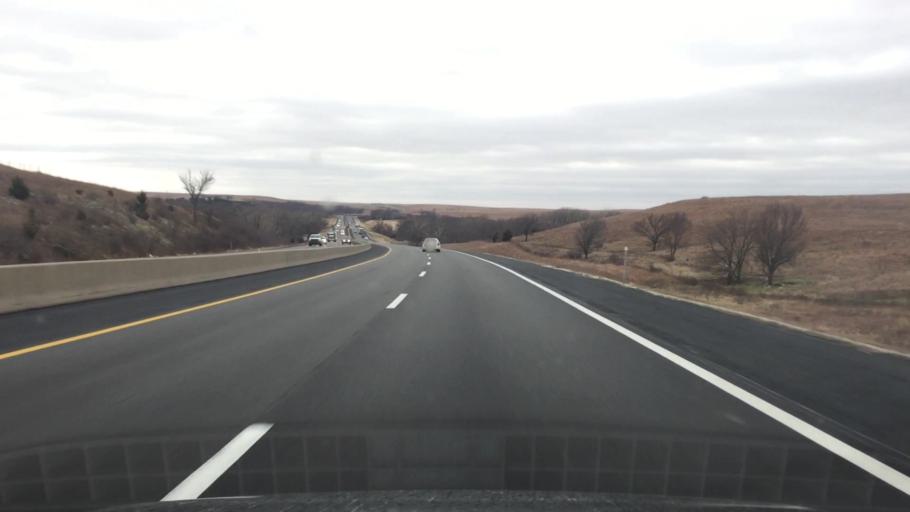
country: US
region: Kansas
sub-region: Chase County
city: Cottonwood Falls
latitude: 38.1331
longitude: -96.5402
